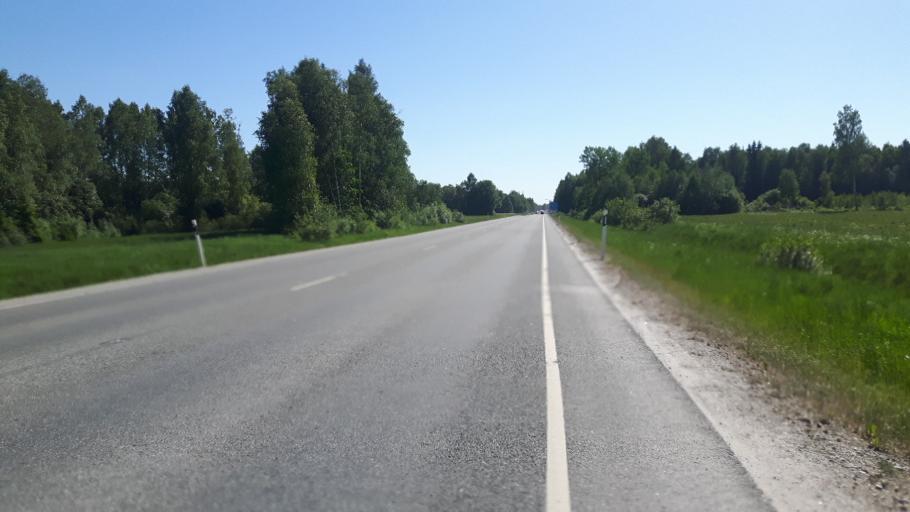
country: EE
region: Raplamaa
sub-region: Rapla vald
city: Rapla
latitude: 59.0204
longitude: 24.8084
